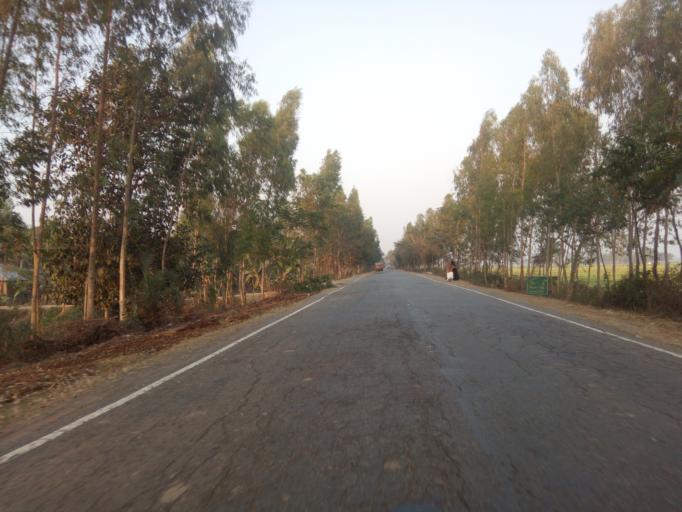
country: BD
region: Rajshahi
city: Bogra
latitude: 24.5712
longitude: 89.2151
